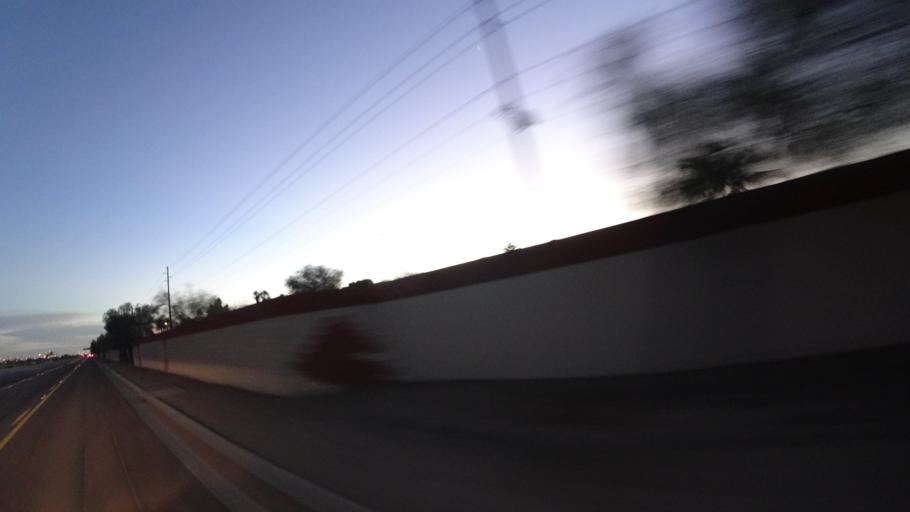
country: US
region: Arizona
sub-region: Maricopa County
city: Scottsdale
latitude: 33.4908
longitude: -111.8918
